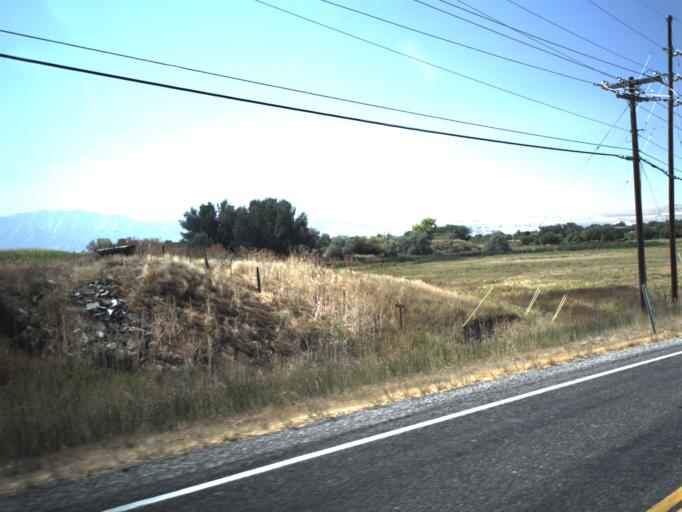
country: US
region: Utah
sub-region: Cache County
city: Smithfield
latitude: 41.8390
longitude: -111.8746
